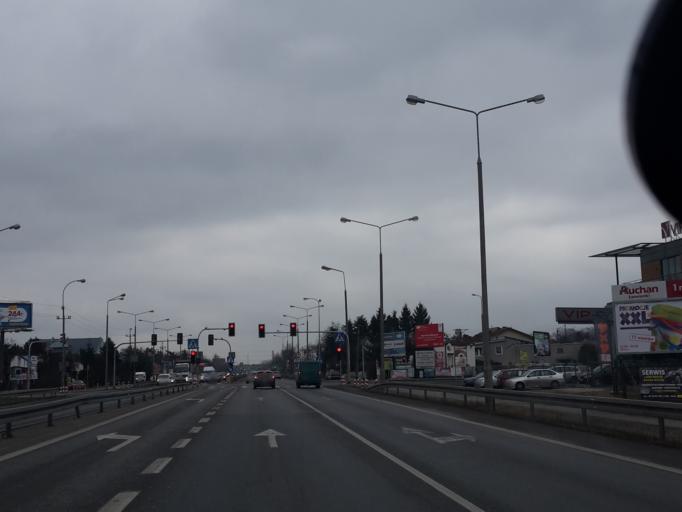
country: PL
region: Masovian Voivodeship
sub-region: Powiat warszawski zachodni
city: Lomianki
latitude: 52.3341
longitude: 20.8856
